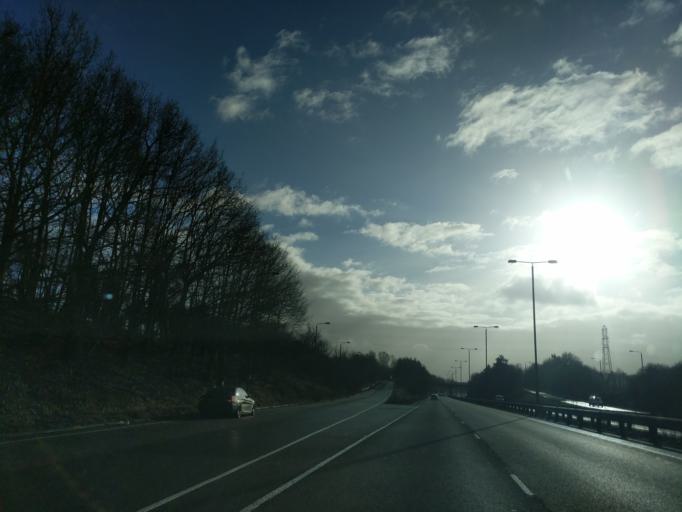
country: GB
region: England
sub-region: Derbyshire
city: Findern
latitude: 52.8894
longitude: -1.5432
